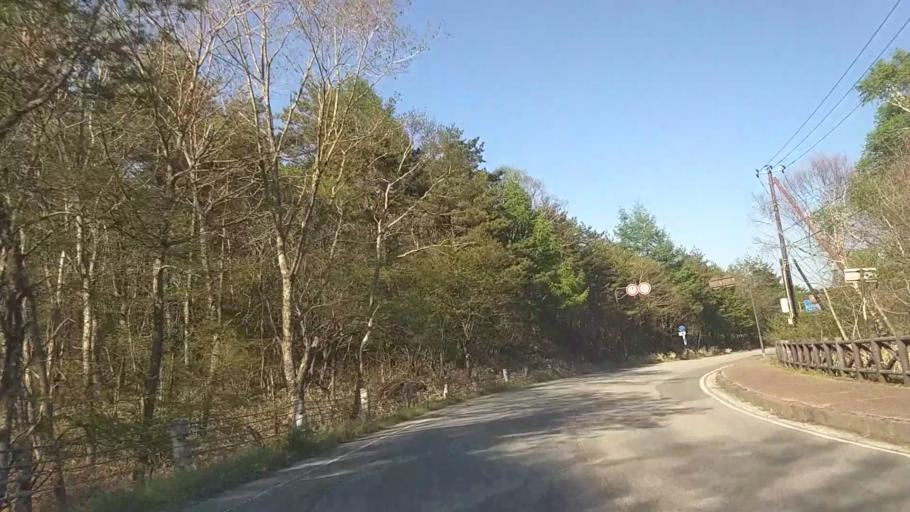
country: JP
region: Yamanashi
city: Nirasaki
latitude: 35.9350
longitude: 138.4216
